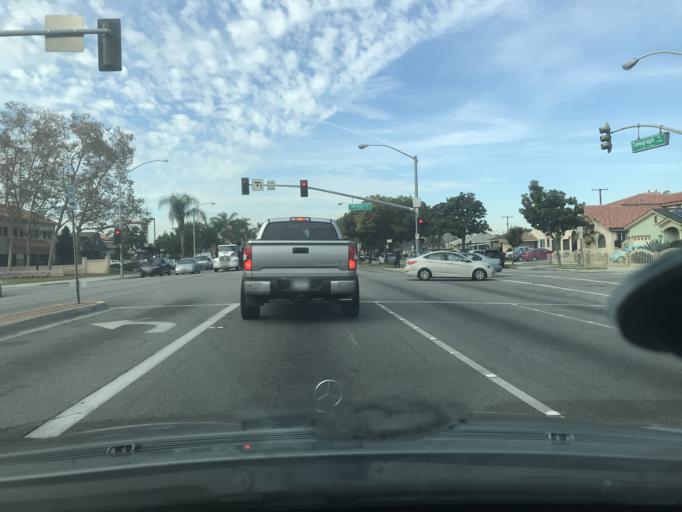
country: US
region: California
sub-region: Los Angeles County
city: Santa Fe Springs
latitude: 33.9472
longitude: -118.0855
